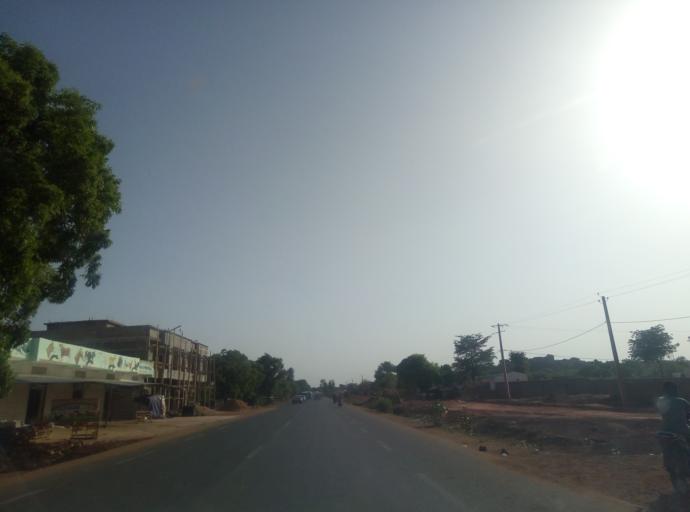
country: ML
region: Bamako
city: Bamako
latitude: 12.5852
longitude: -7.7701
